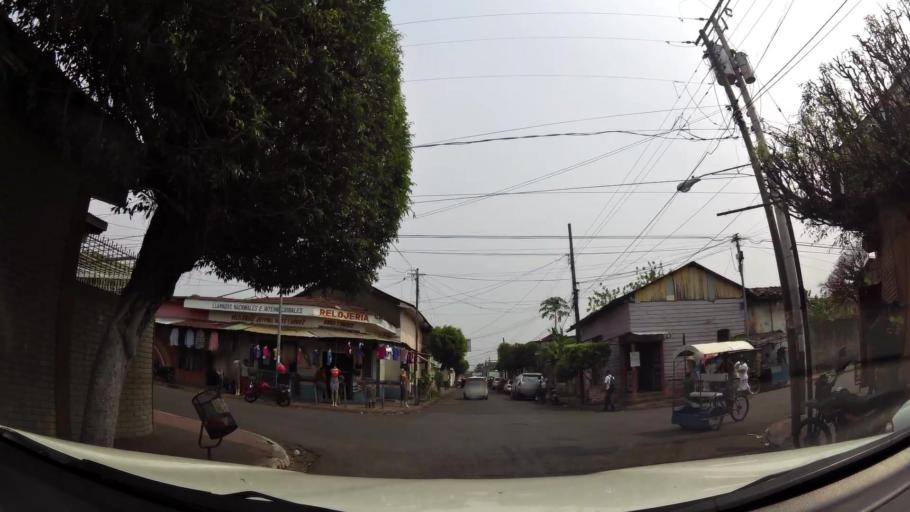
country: NI
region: Chinandega
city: Chinandega
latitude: 12.6288
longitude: -87.1314
